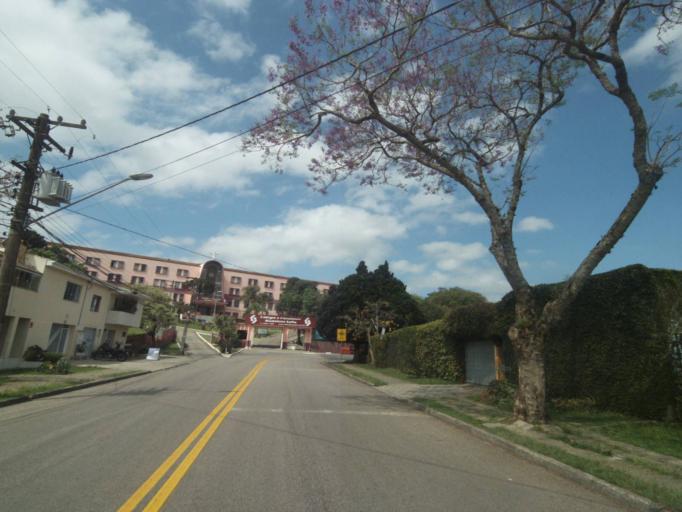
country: BR
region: Parana
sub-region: Pinhais
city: Pinhais
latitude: -25.4128
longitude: -49.2158
